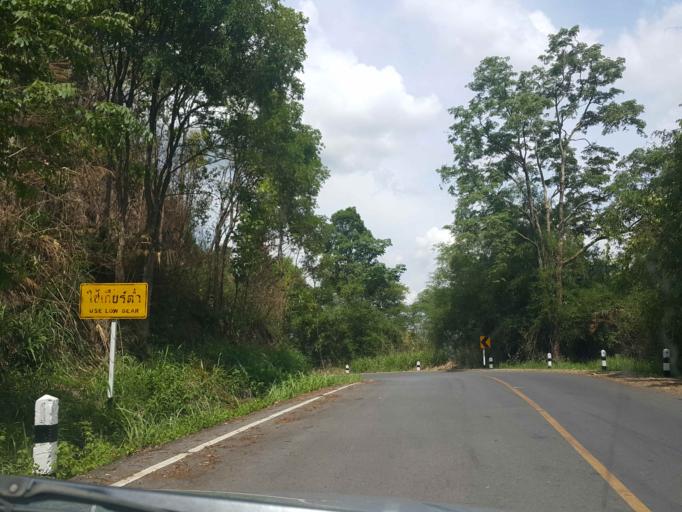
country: TH
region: Nan
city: Ban Luang
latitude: 18.8757
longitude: 100.5323
